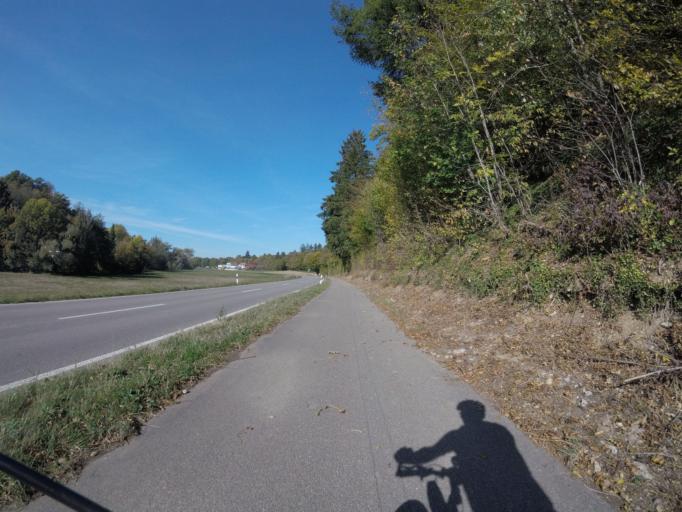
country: DE
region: Baden-Wuerttemberg
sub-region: Karlsruhe Region
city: Bretten
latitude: 49.0201
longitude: 8.7174
